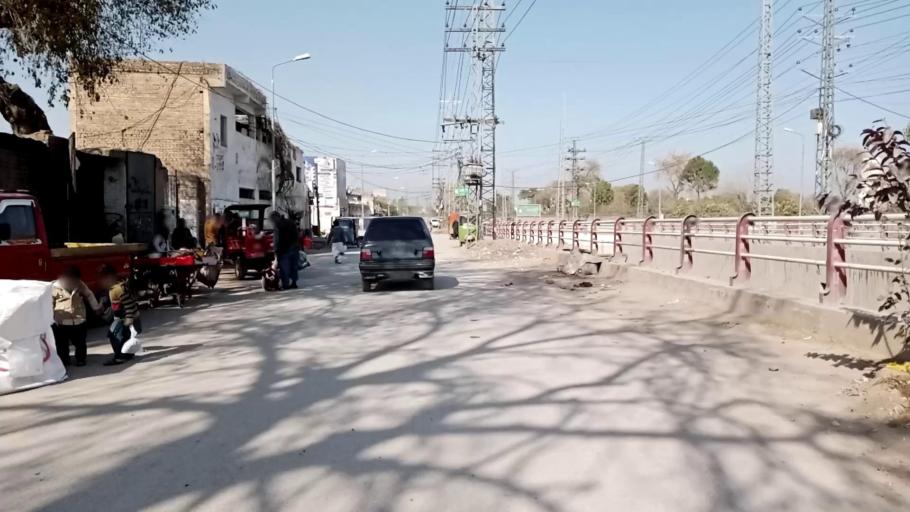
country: PK
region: Khyber Pakhtunkhwa
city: Peshawar
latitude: 33.9914
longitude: 71.4848
